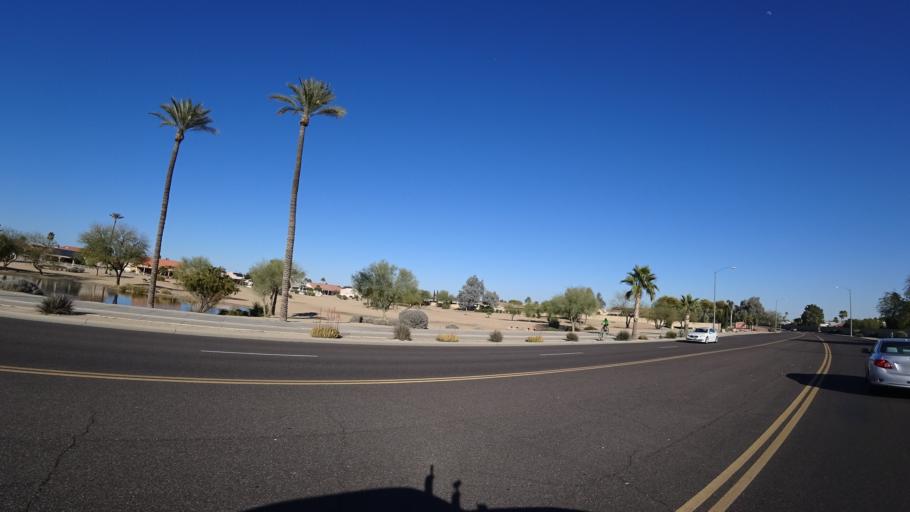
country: US
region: Arizona
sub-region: Maricopa County
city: Sun City West
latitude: 33.6823
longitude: -112.3529
